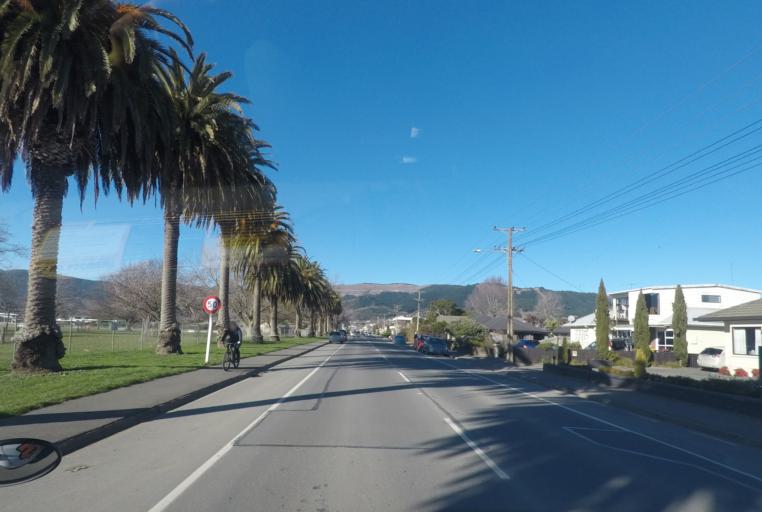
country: NZ
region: Tasman
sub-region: Tasman District
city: Richmond
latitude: -41.3336
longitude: 173.1785
